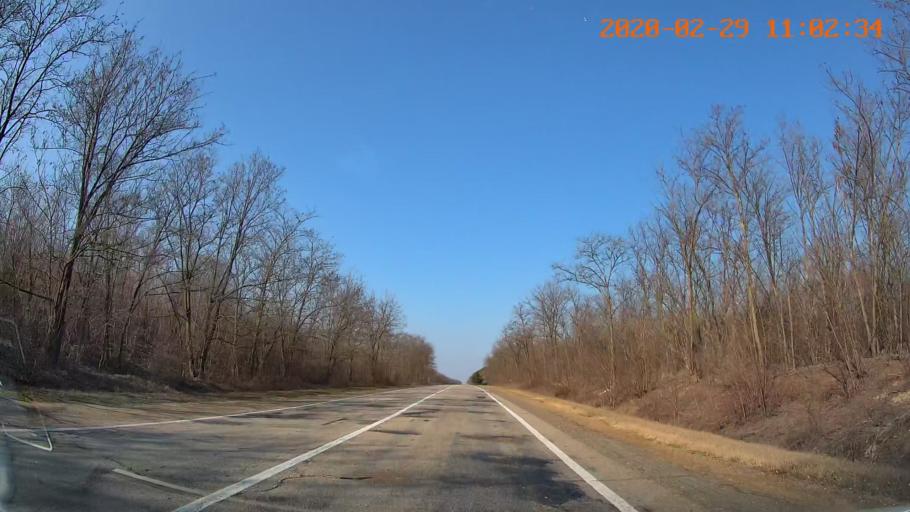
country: MD
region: Telenesti
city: Grigoriopol
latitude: 47.1734
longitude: 29.2354
